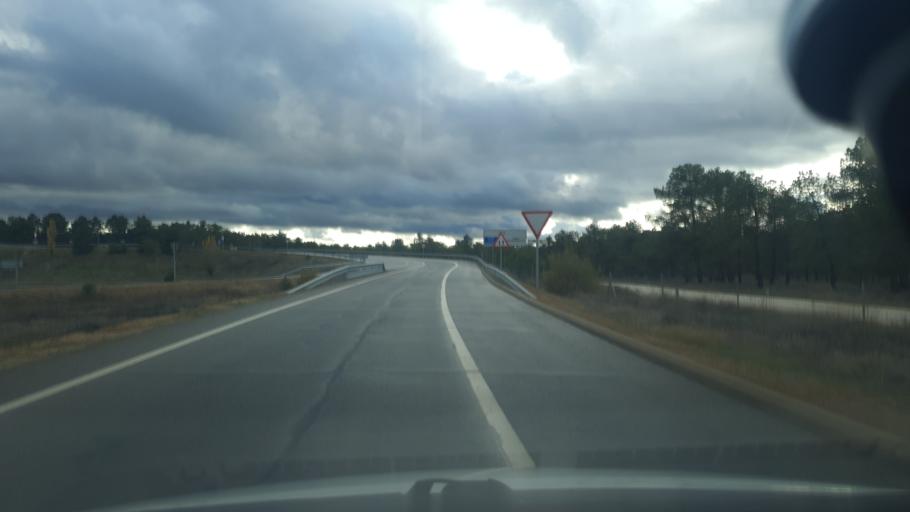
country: ES
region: Castille and Leon
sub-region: Provincia de Segovia
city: Sanchonuno
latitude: 41.2961
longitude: -4.3012
